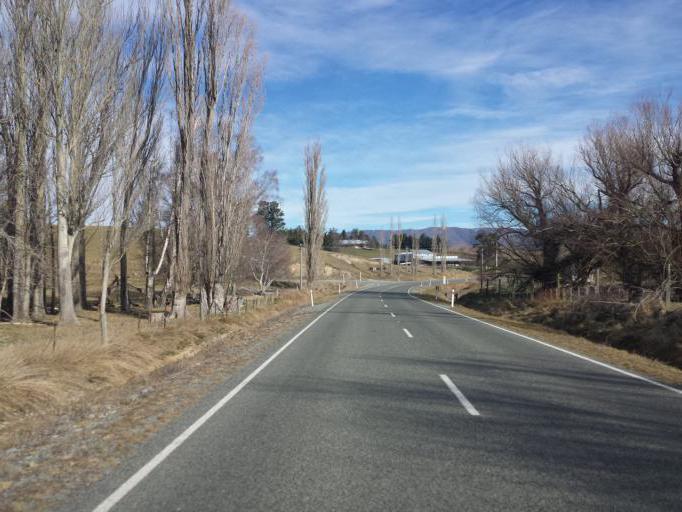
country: NZ
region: Canterbury
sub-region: Timaru District
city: Pleasant Point
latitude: -44.0652
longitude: 170.8843
